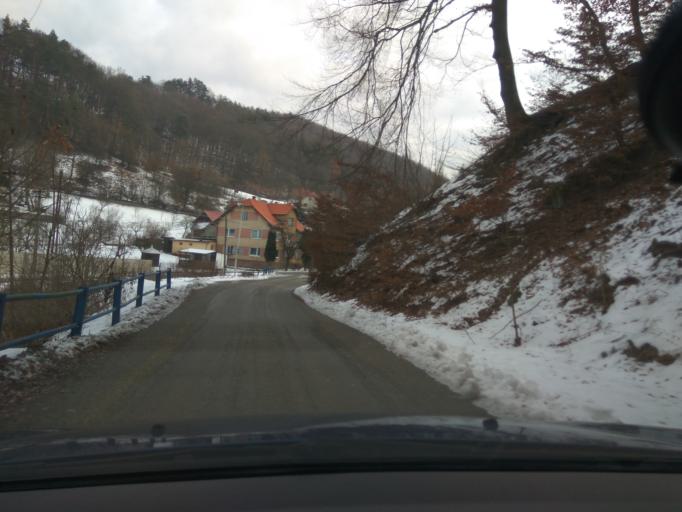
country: SK
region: Banskobystricky
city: Zarnovica
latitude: 48.4848
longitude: 18.7357
